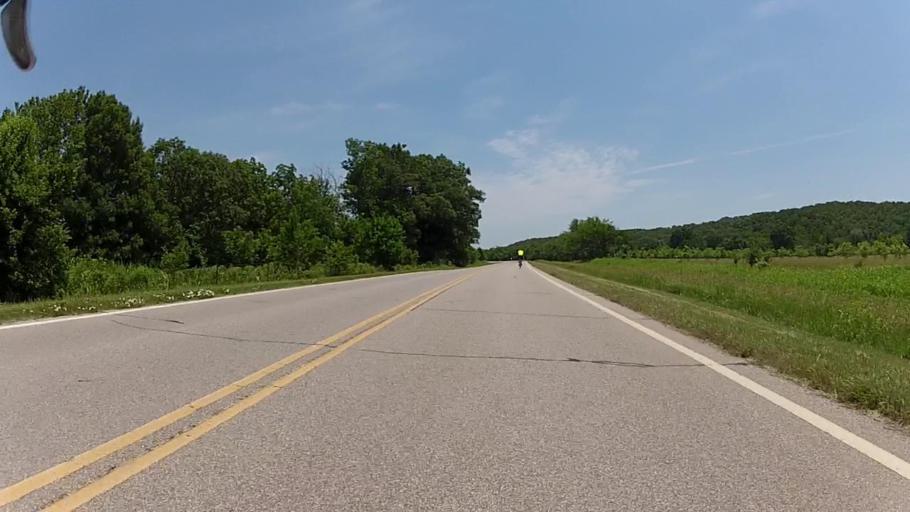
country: US
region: Kansas
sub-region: Chautauqua County
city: Sedan
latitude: 37.1197
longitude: -96.2224
